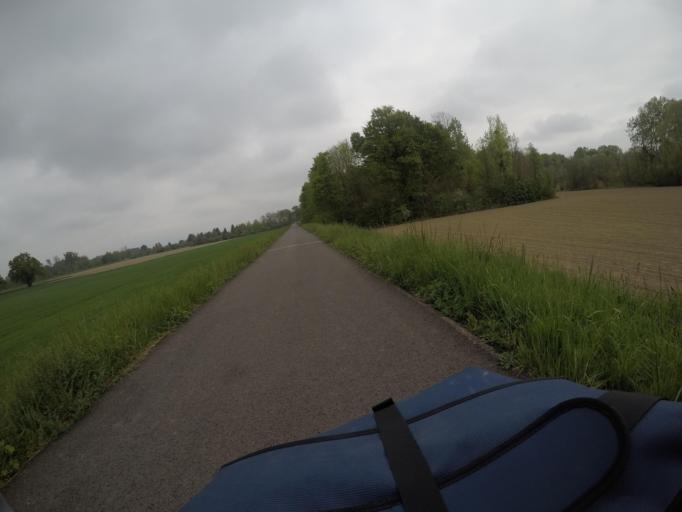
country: FR
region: Alsace
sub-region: Departement du Bas-Rhin
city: La Wantzenau
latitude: 48.6431
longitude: 7.8255
